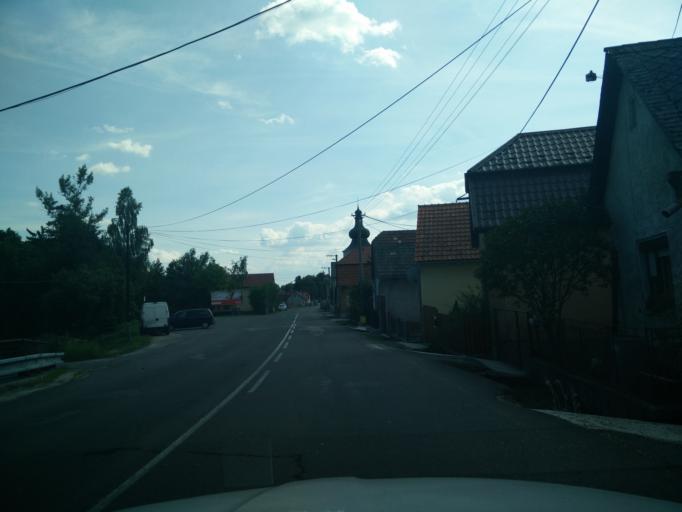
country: SK
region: Nitriansky
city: Prievidza
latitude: 48.8974
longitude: 18.6438
